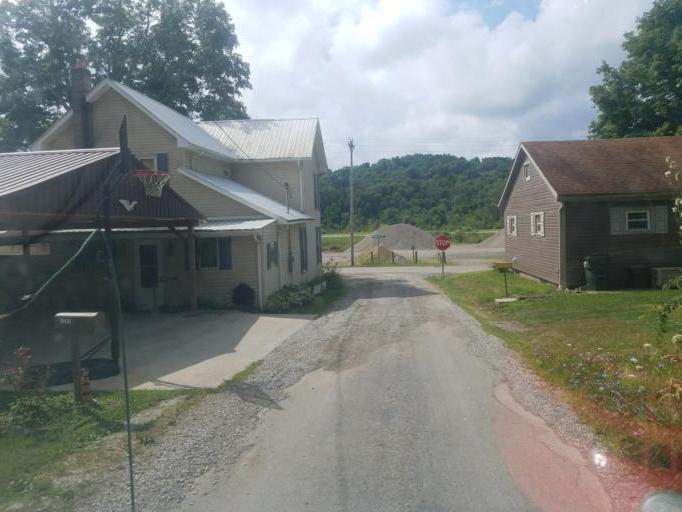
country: US
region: Ohio
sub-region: Belmont County
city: Barnesville
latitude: 40.0510
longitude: -81.3397
